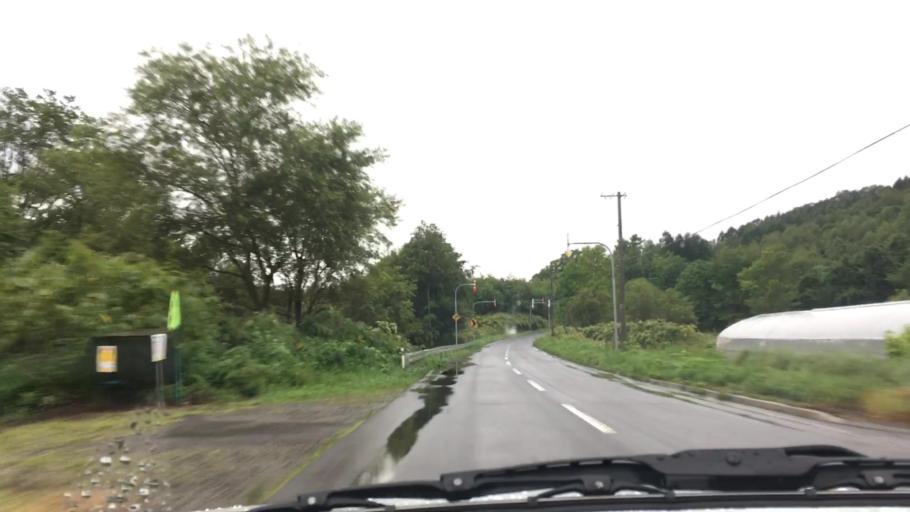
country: JP
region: Hokkaido
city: Niseko Town
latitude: 42.6574
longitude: 140.7441
